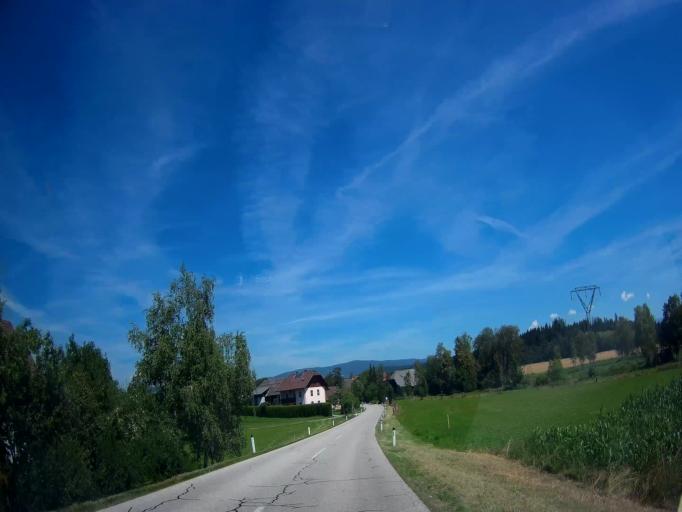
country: AT
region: Carinthia
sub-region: Politischer Bezirk Sankt Veit an der Glan
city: St. Georgen am Laengsee
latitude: 46.7989
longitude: 14.4137
